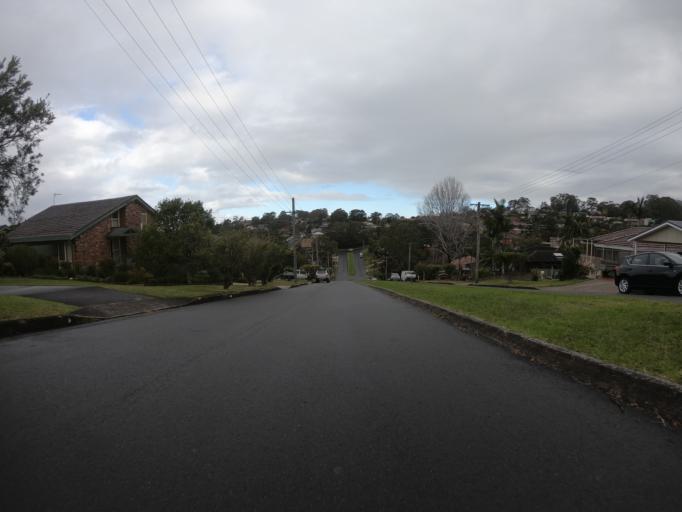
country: AU
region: New South Wales
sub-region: Wollongong
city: Mount Keira
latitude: -34.4240
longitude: 150.8554
